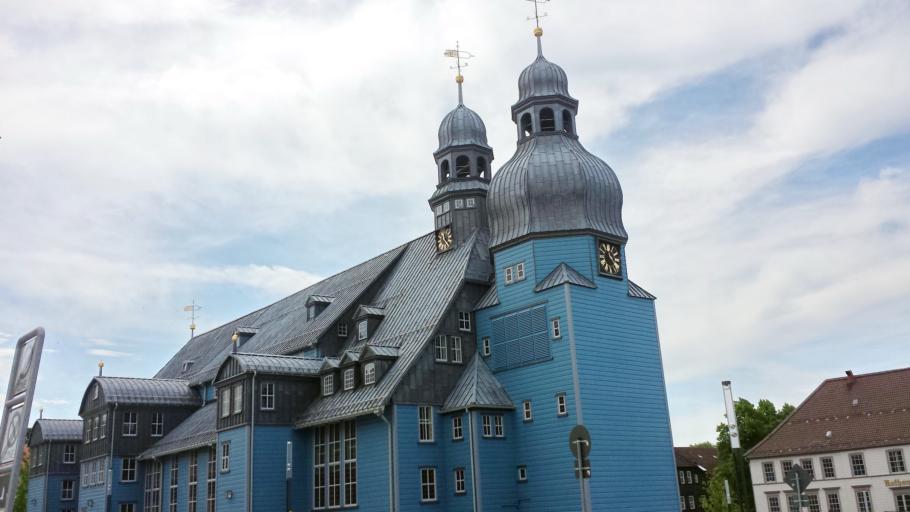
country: DE
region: Lower Saxony
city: Clausthal-Zellerfeld
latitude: 51.8043
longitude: 10.3334
